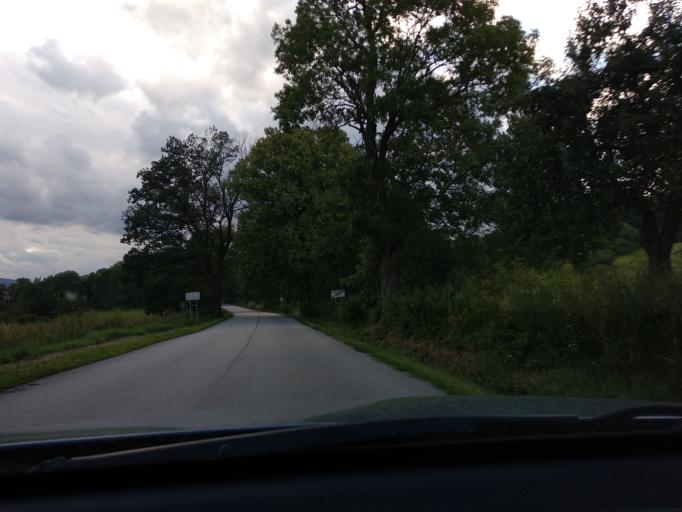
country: SK
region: Zilinsky
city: Ruzomberok
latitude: 49.1005
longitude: 19.4015
